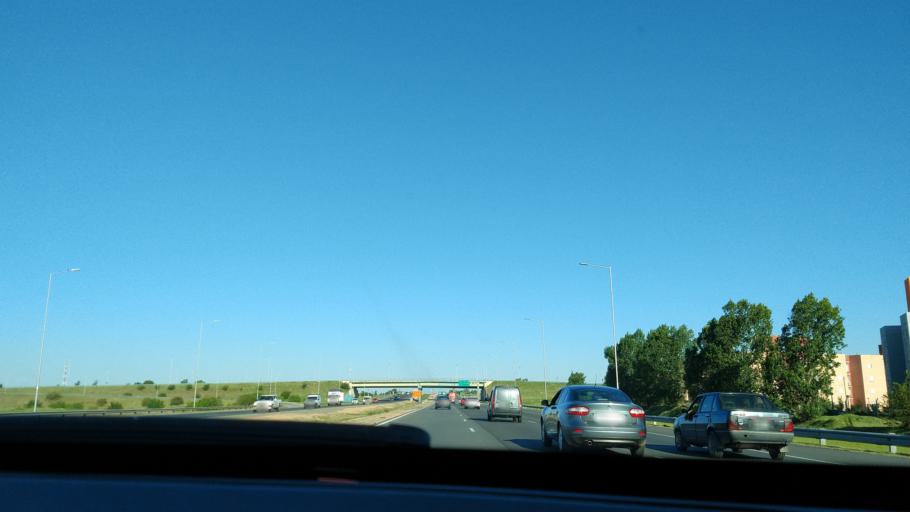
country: AR
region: Cordoba
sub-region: Departamento de Capital
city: Cordoba
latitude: -31.3538
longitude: -64.1928
